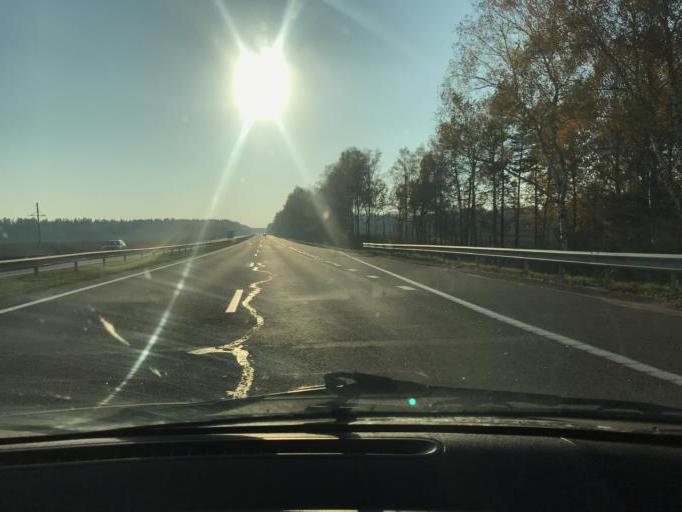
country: BY
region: Minsk
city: Loshnitsa
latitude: 54.2855
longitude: 28.7434
